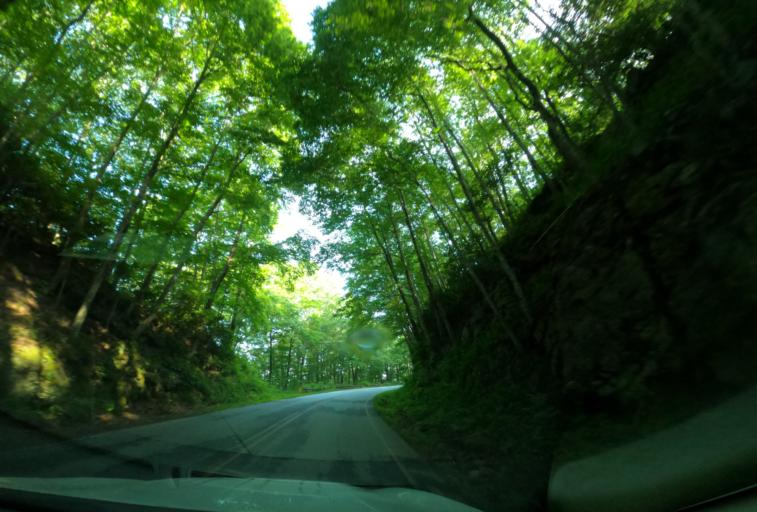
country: US
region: North Carolina
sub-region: Transylvania County
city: Brevard
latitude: 35.2628
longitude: -82.9221
